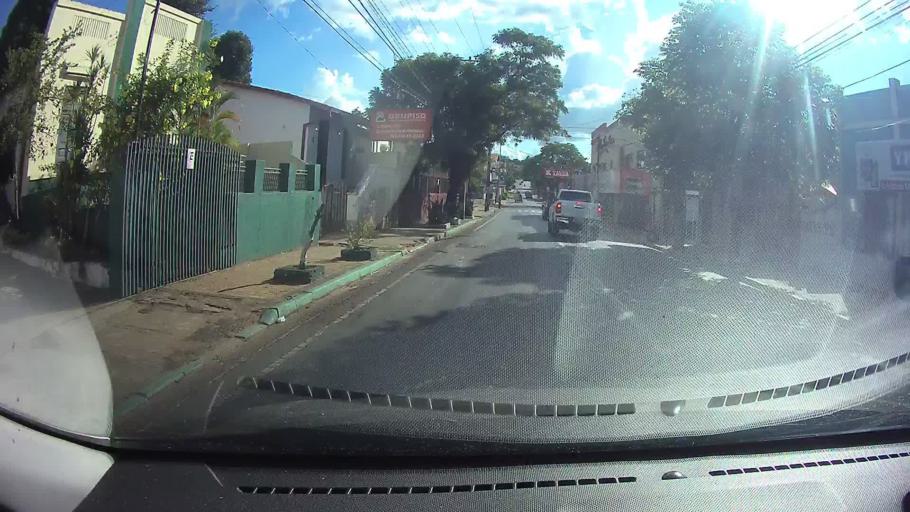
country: PY
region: Cordillera
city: Caacupe
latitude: -25.3863
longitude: -57.1443
